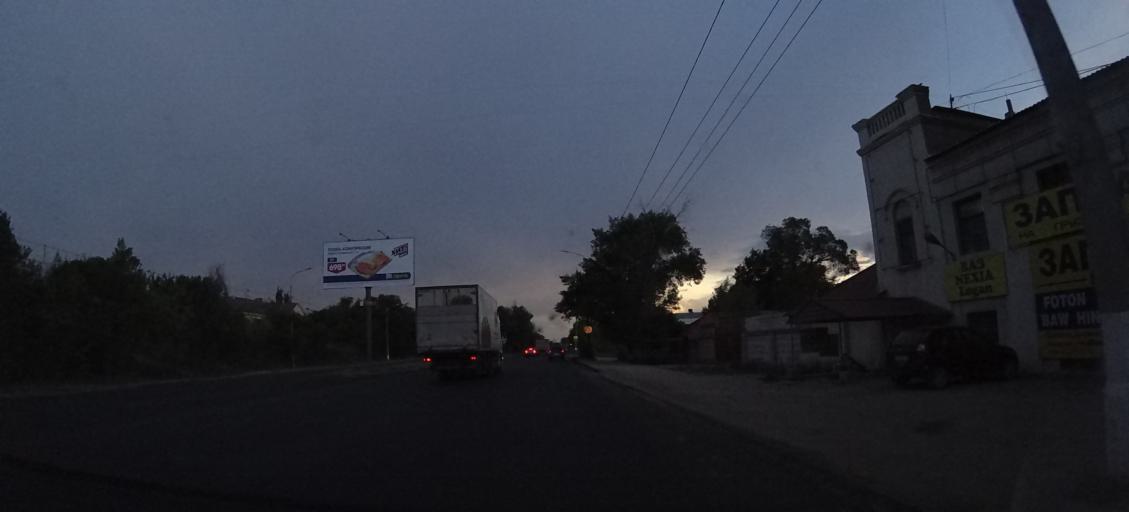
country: RU
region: Volgograd
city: Volgograd
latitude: 48.5527
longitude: 44.4469
